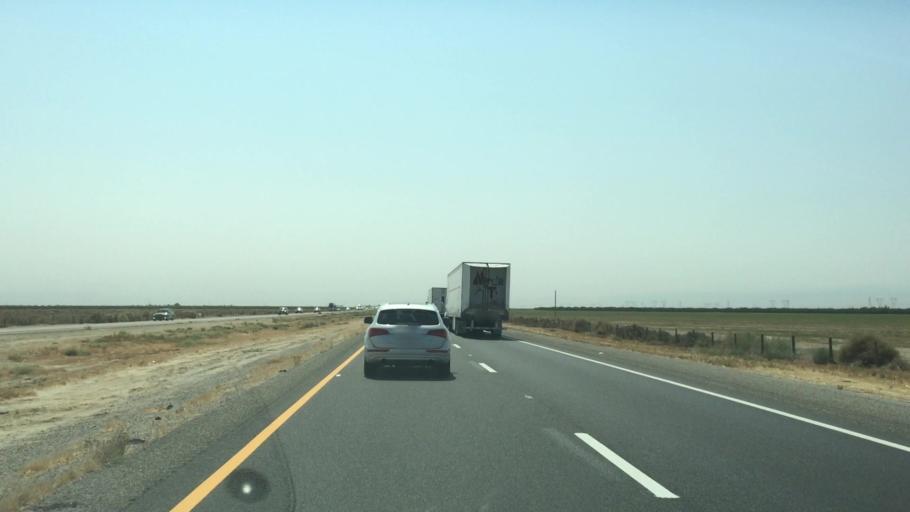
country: US
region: California
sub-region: Kern County
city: Buttonwillow
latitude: 35.3763
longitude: -119.3664
